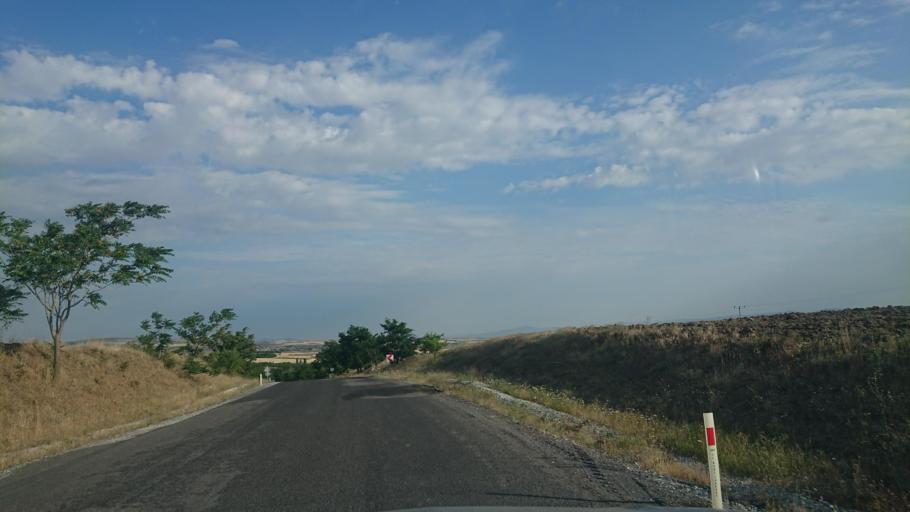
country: TR
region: Aksaray
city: Ortakoy
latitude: 38.8123
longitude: 34.0541
